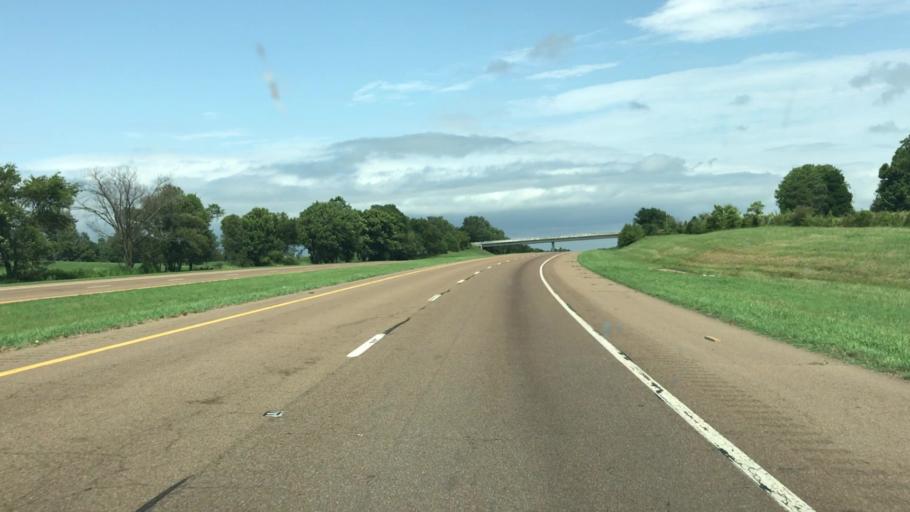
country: US
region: Tennessee
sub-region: Obion County
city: South Fulton
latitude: 36.4748
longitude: -88.9602
